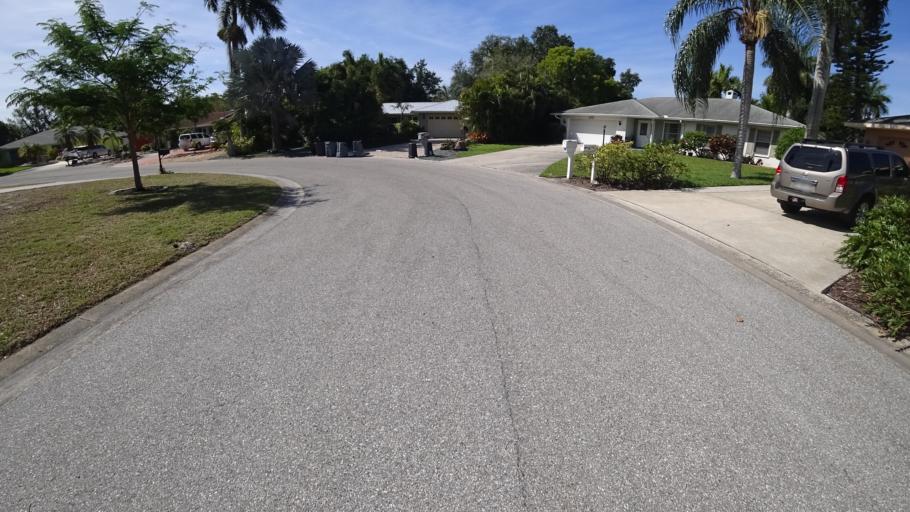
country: US
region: Florida
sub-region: Manatee County
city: West Bradenton
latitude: 27.5113
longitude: -82.6347
